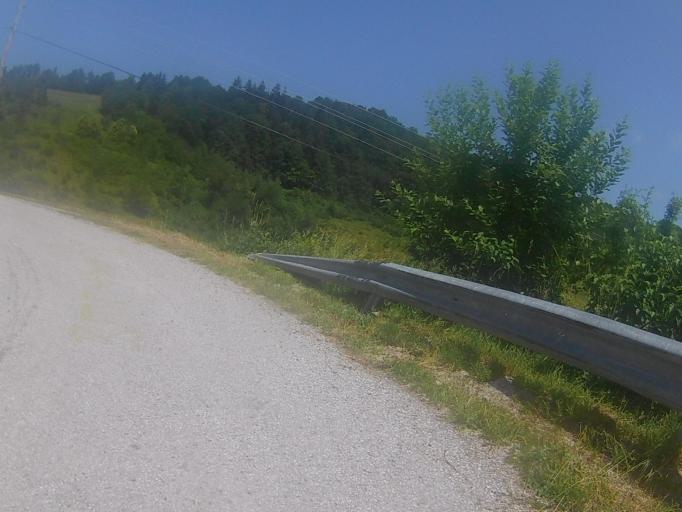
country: SI
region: Kungota
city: Zgornja Kungota
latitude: 46.6221
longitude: 15.5717
